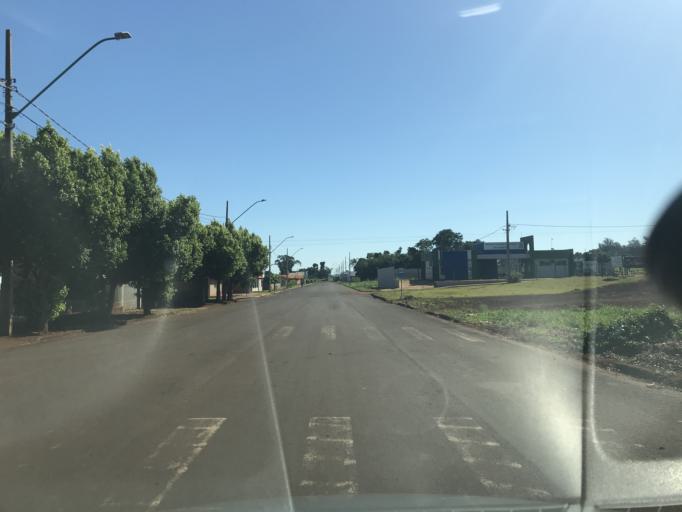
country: BR
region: Parana
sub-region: Palotina
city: Palotina
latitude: -24.2677
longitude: -53.8451
